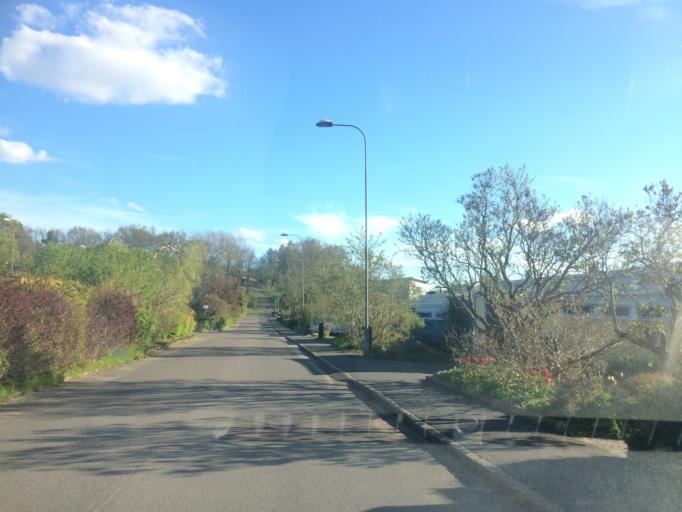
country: SE
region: Vaestra Goetaland
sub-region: Goteborg
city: Goeteborg
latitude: 57.7590
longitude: 11.9307
